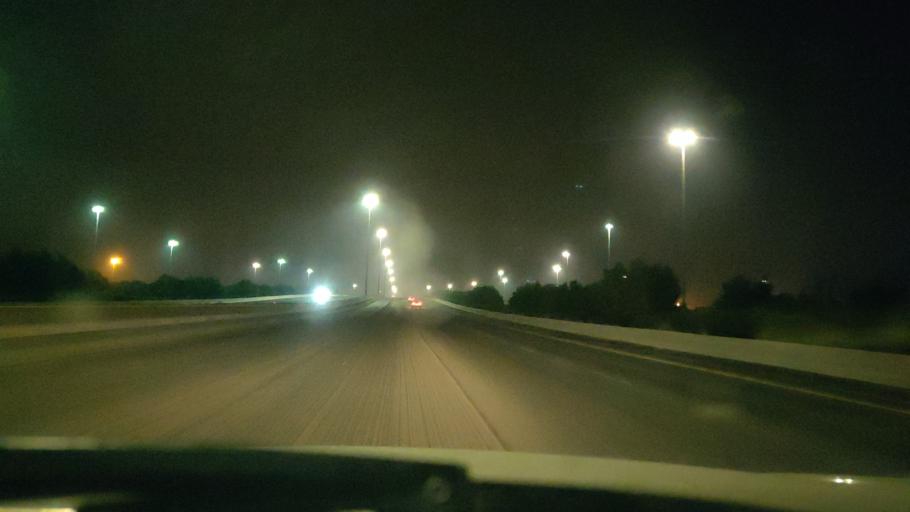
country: KW
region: Muhafazat al Jahra'
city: Al Jahra'
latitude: 29.3256
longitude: 47.7462
